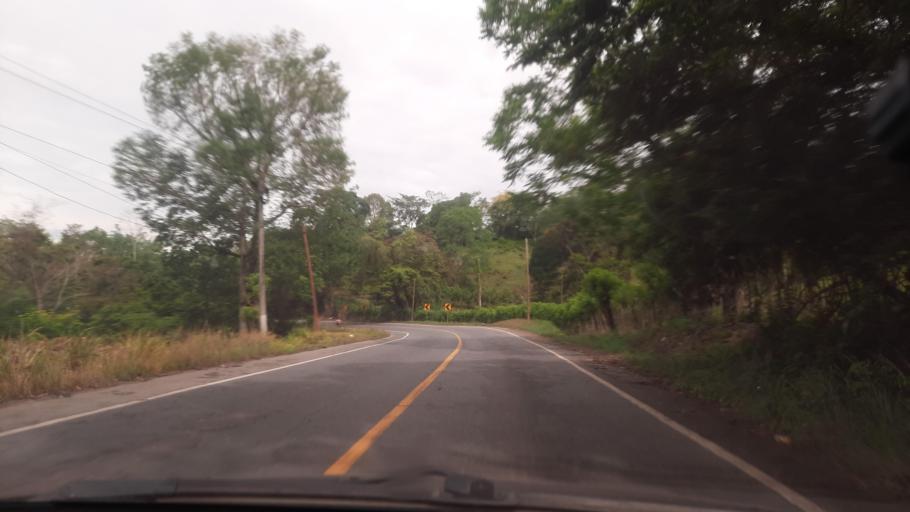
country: GT
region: Izabal
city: Morales
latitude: 15.5224
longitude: -88.7945
